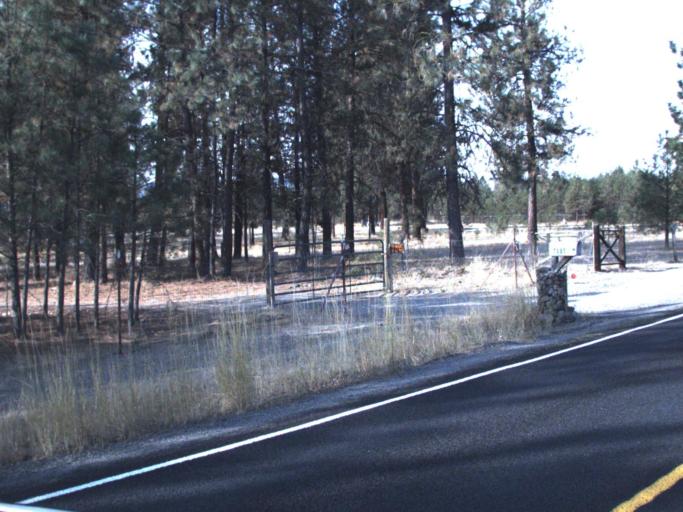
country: US
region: Washington
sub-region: Spokane County
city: Fairchild Air Force Base
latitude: 47.8393
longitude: -117.7924
